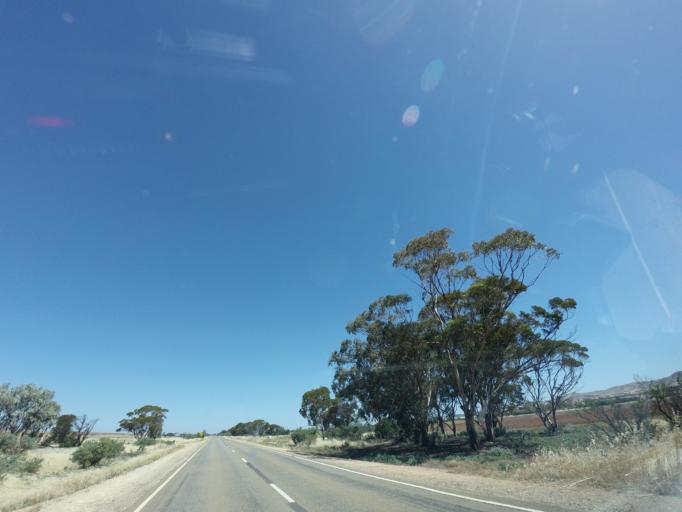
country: AU
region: South Australia
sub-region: Peterborough
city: Peterborough
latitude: -32.7823
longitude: 138.6683
